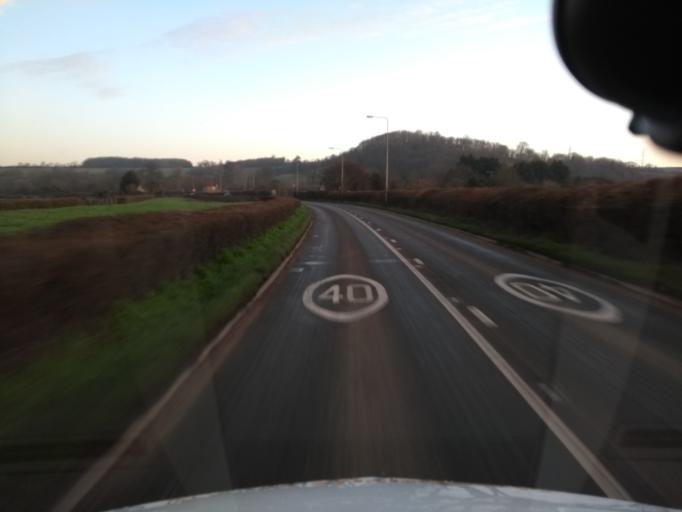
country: GB
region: England
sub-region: Somerset
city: Puriton
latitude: 51.1519
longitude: -2.9600
